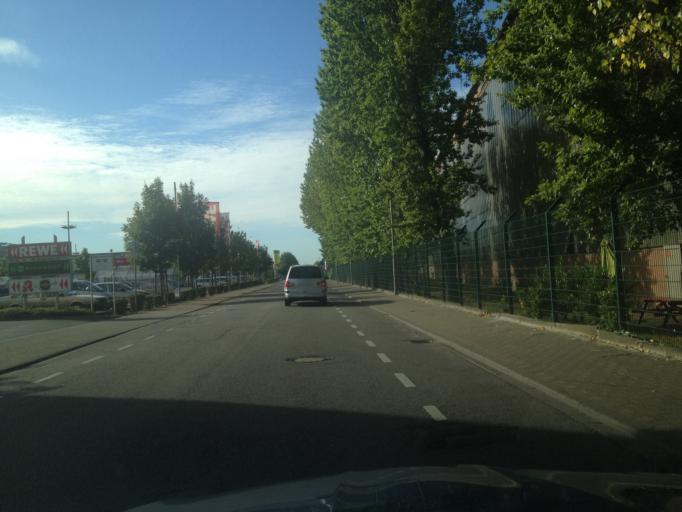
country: DE
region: Baden-Wuerttemberg
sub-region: Karlsruhe Region
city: Schwetzingen
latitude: 49.3809
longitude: 8.5828
